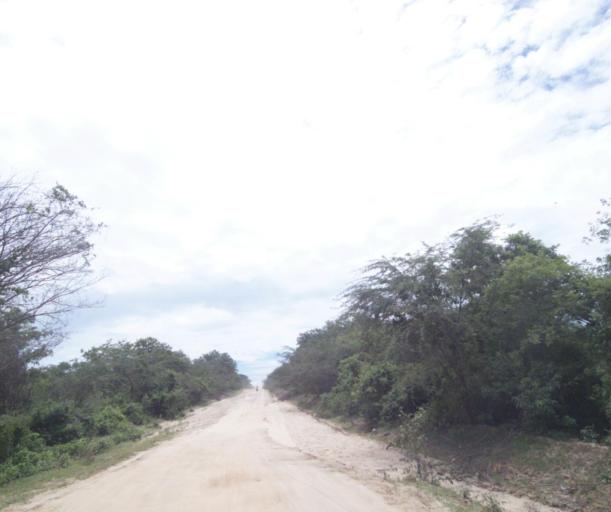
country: BR
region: Bahia
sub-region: Carinhanha
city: Carinhanha
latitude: -14.2129
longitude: -43.8968
